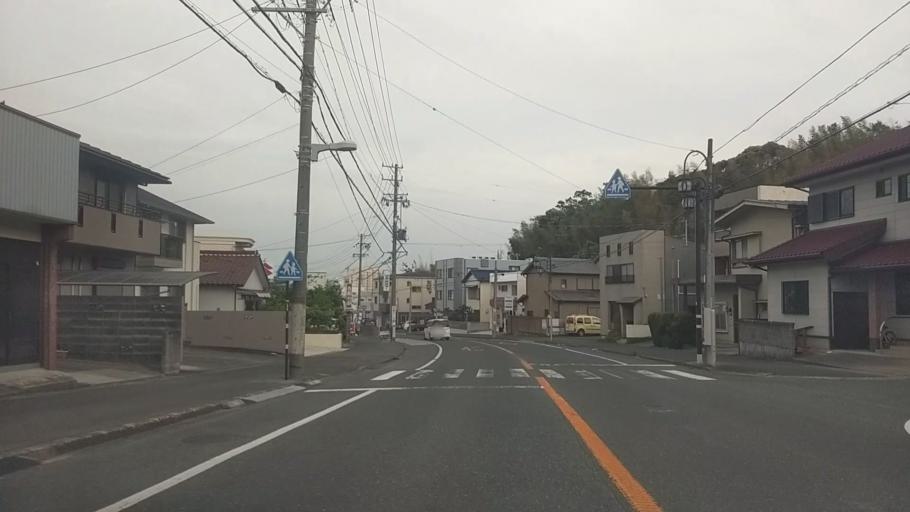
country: JP
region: Shizuoka
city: Hamamatsu
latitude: 34.7261
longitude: 137.6936
